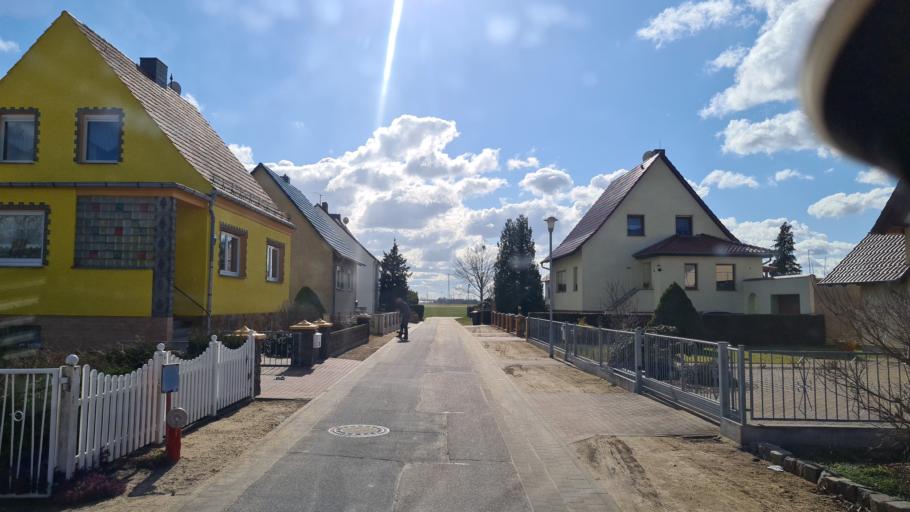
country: DE
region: Brandenburg
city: Falkenberg
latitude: 51.5844
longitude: 13.2156
